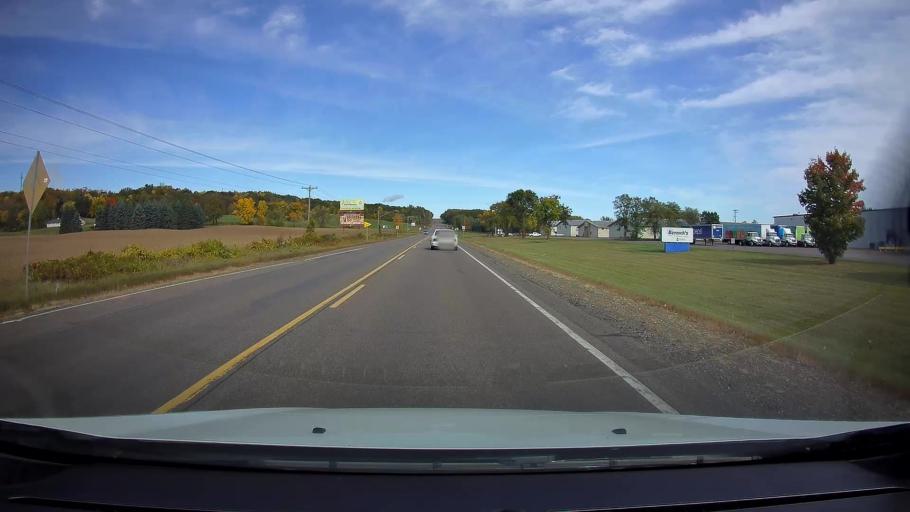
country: US
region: Wisconsin
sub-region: Polk County
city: Saint Croix Falls
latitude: 45.3619
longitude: -92.6366
